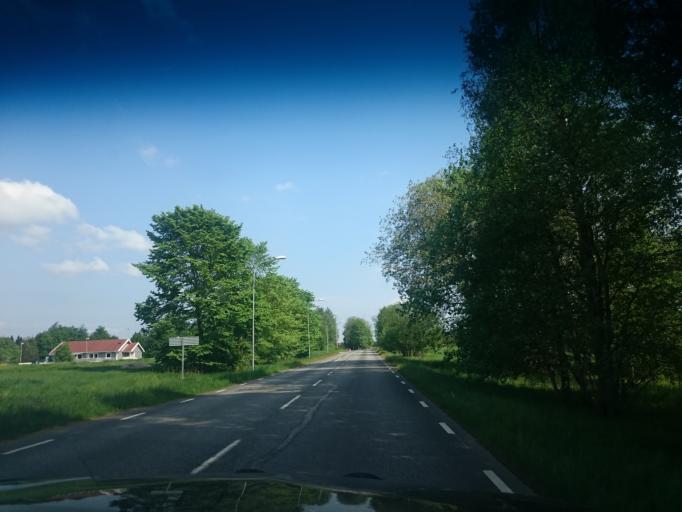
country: SE
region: Joenkoeping
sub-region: Vetlanda Kommun
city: Landsbro
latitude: 57.3821
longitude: 14.9691
